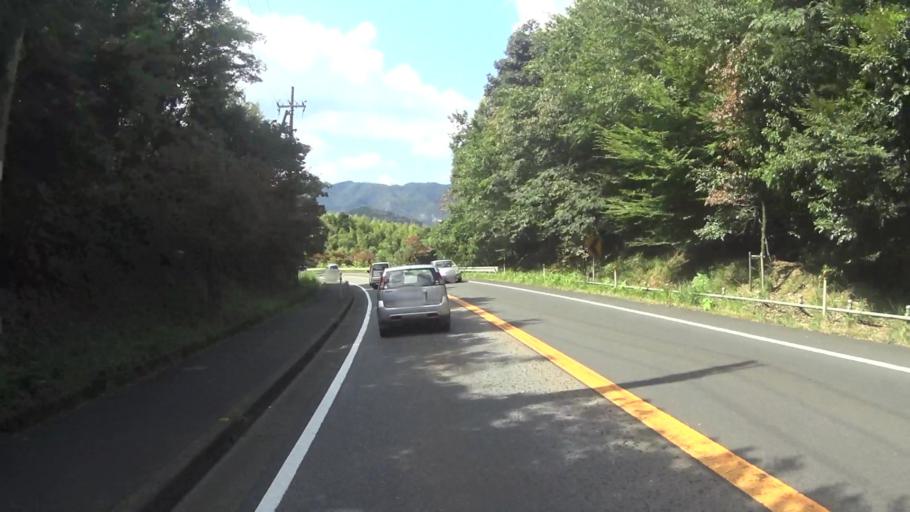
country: JP
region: Kyoto
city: Miyazu
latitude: 35.5520
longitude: 135.1652
